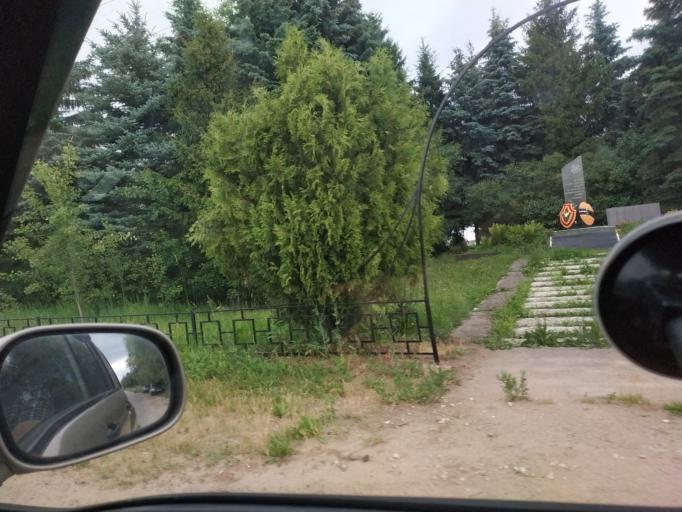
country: RU
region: Moskovskaya
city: Krasnoarmeysk
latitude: 56.0886
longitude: 38.2258
